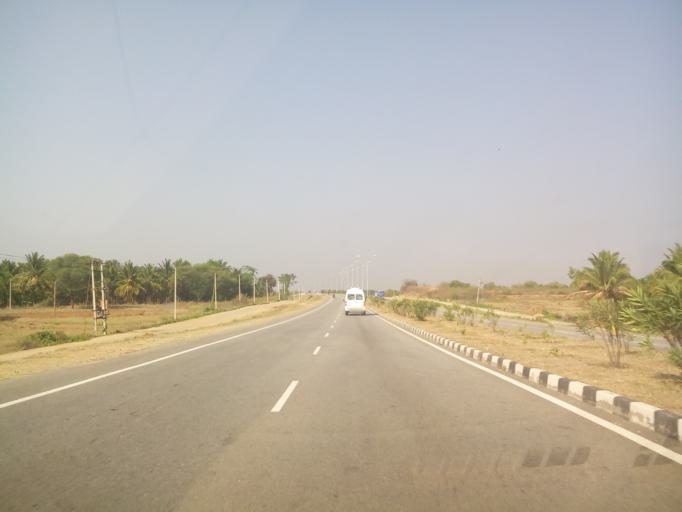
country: IN
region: Karnataka
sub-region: Tumkur
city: Kunigal
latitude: 13.0192
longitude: 77.0489
